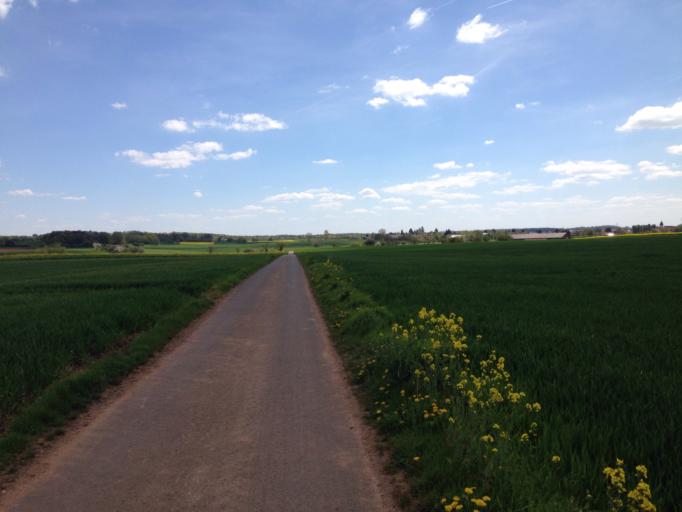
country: DE
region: Hesse
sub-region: Regierungsbezirk Giessen
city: Lich
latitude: 50.5074
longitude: 8.8493
